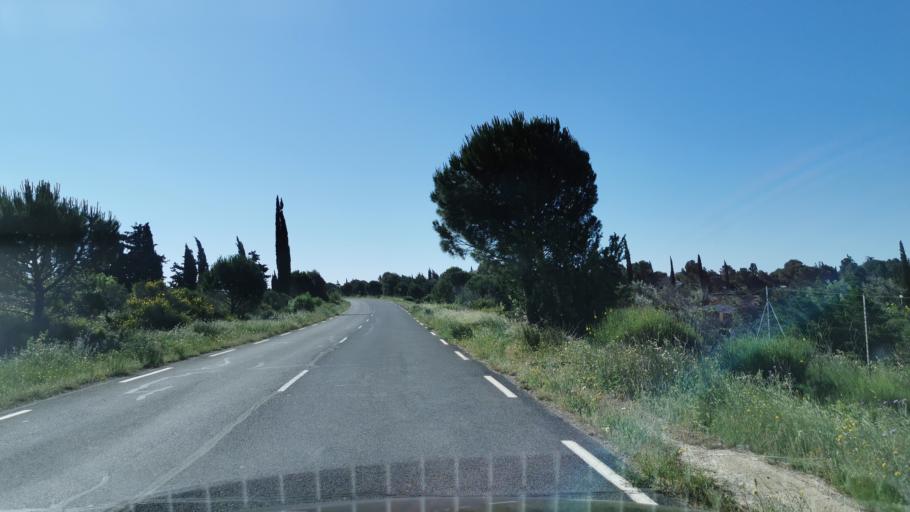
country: FR
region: Languedoc-Roussillon
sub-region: Departement de l'Aude
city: Narbonne
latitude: 43.1496
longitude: 3.0011
